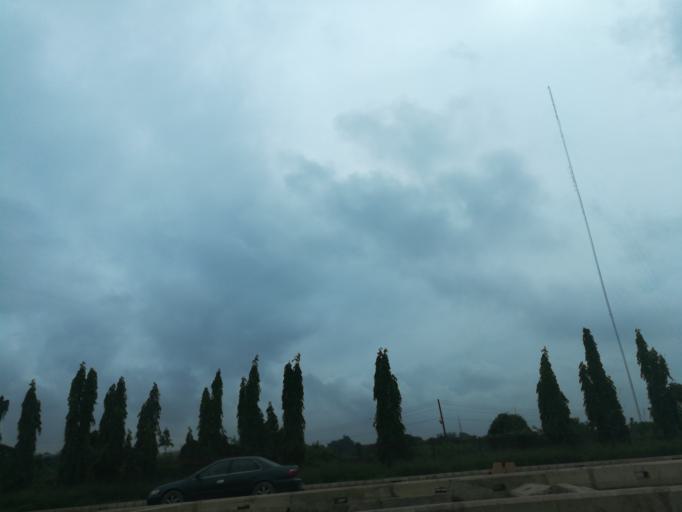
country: NG
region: Lagos
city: Oshodi
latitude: 6.5697
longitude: 3.3460
